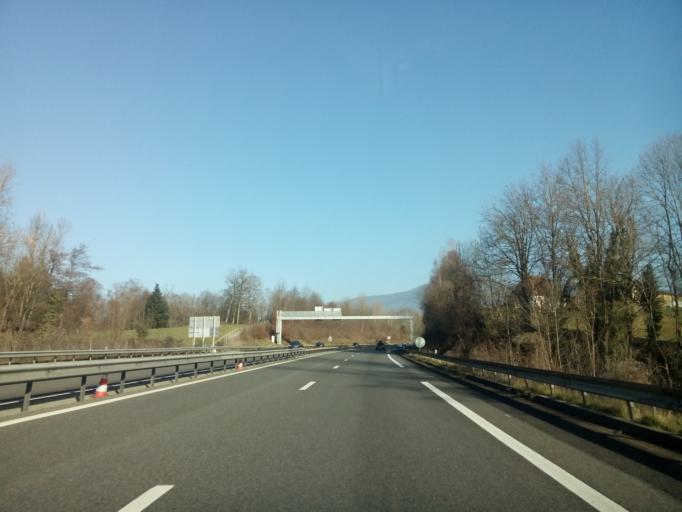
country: FR
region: Rhone-Alpes
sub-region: Departement de la Savoie
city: La Bridoire
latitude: 45.5576
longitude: 5.7583
